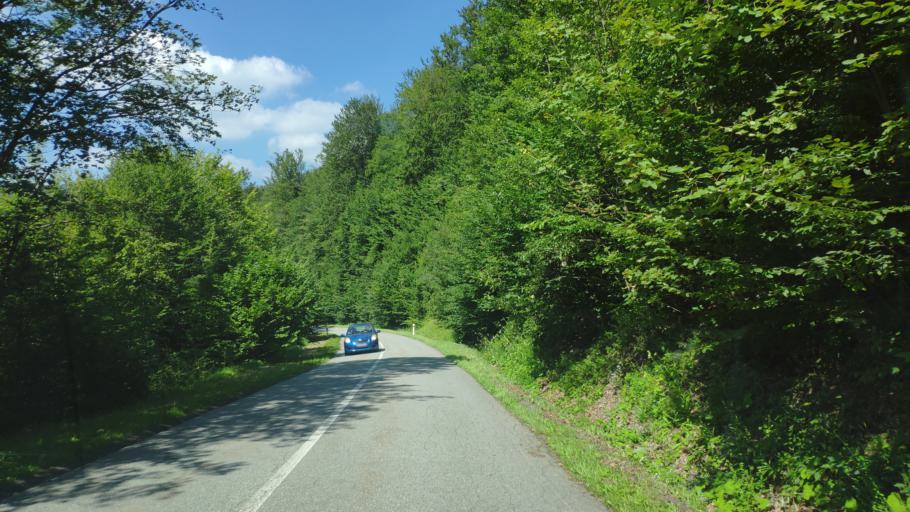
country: PL
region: Subcarpathian Voivodeship
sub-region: Powiat leski
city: Cisna
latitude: 49.0686
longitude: 22.3863
